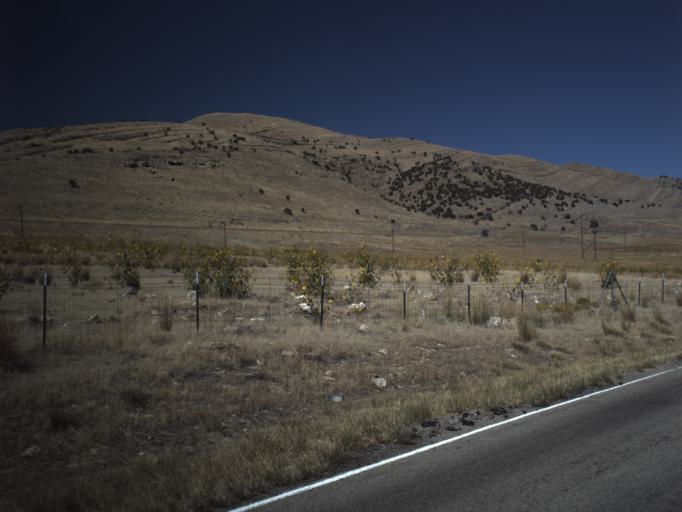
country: US
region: Utah
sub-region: Utah County
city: Saratoga Springs
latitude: 40.1951
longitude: -111.9046
